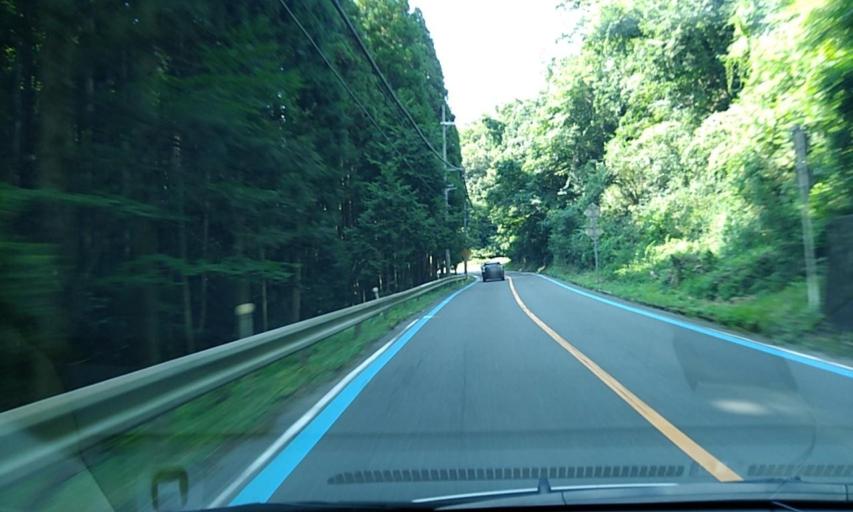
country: JP
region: Kyoto
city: Ayabe
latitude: 35.3055
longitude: 135.2946
